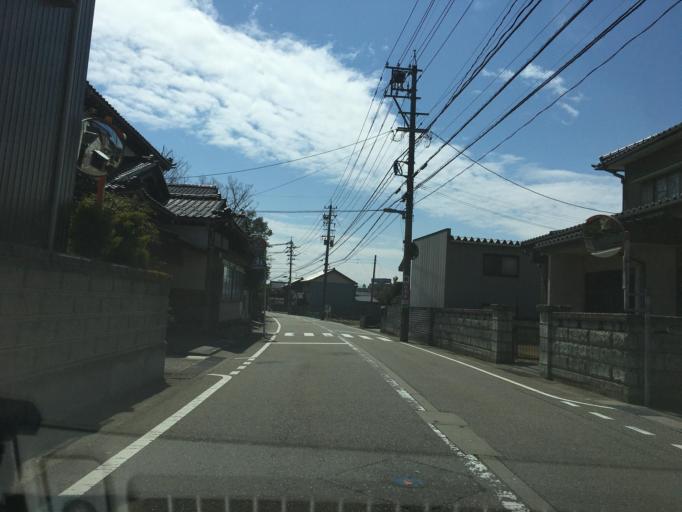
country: JP
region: Toyama
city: Himi
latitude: 36.8449
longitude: 136.9872
